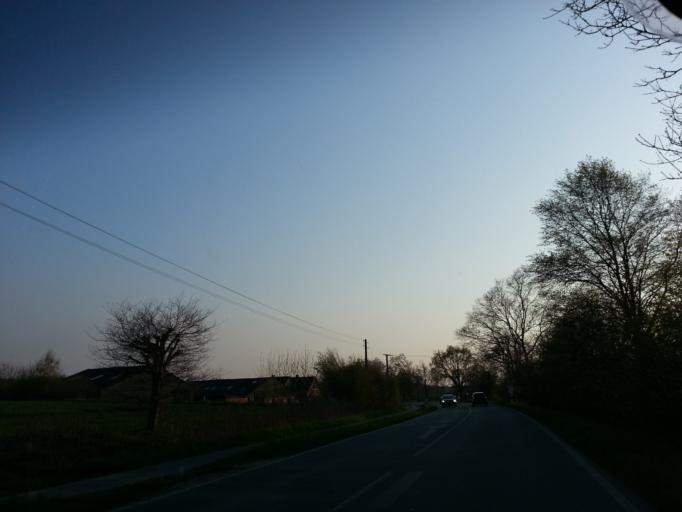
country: DE
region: Schleswig-Holstein
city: Timmendorfer Strand
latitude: 53.9661
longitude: 10.7627
